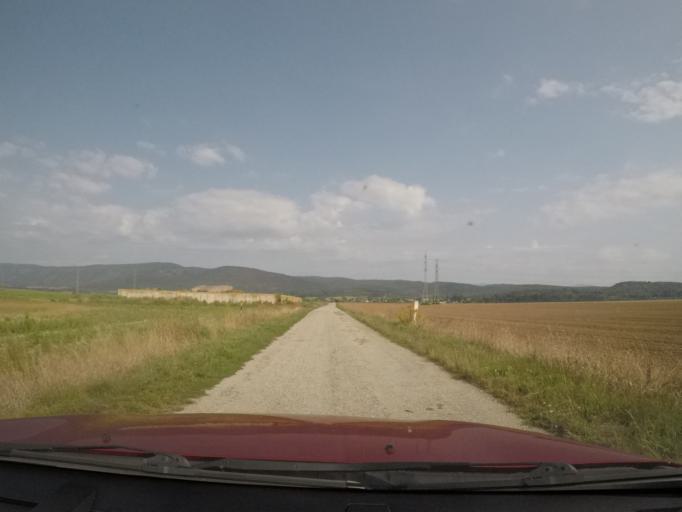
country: SK
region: Kosicky
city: Moldava nad Bodvou
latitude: 48.5956
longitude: 20.9558
